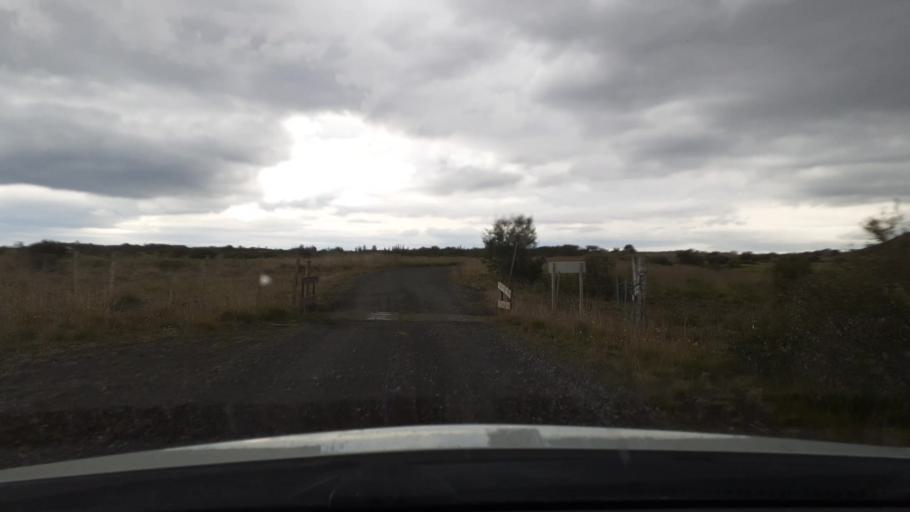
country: IS
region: West
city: Borgarnes
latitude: 64.6385
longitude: -21.7457
